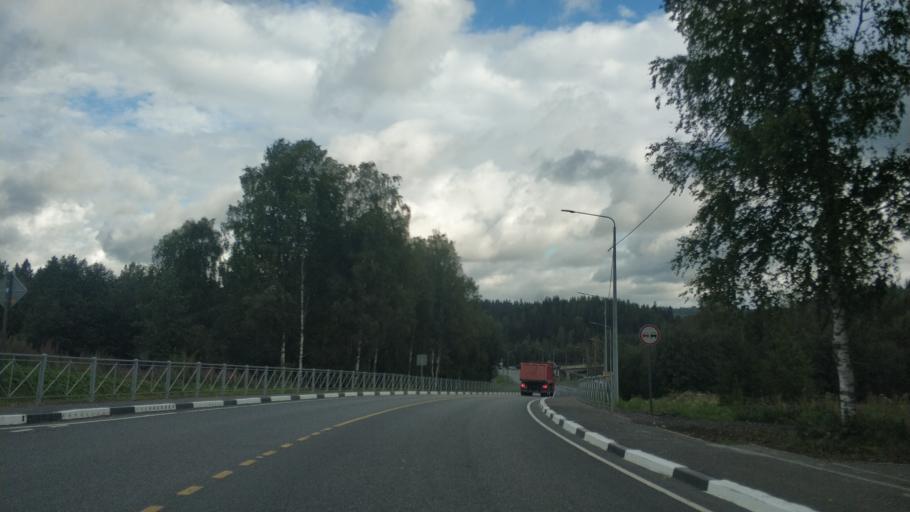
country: RU
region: Republic of Karelia
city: Ruskeala
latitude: 61.9346
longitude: 30.5912
